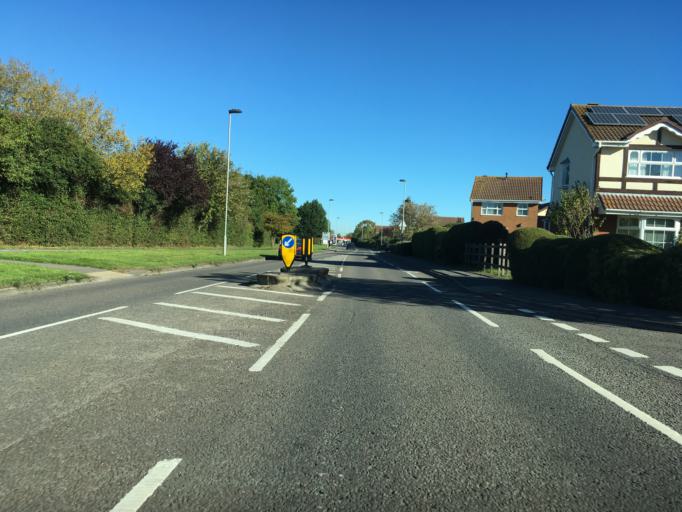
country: GB
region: England
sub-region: South Gloucestershire
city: Yate
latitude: 51.5360
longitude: -2.4094
